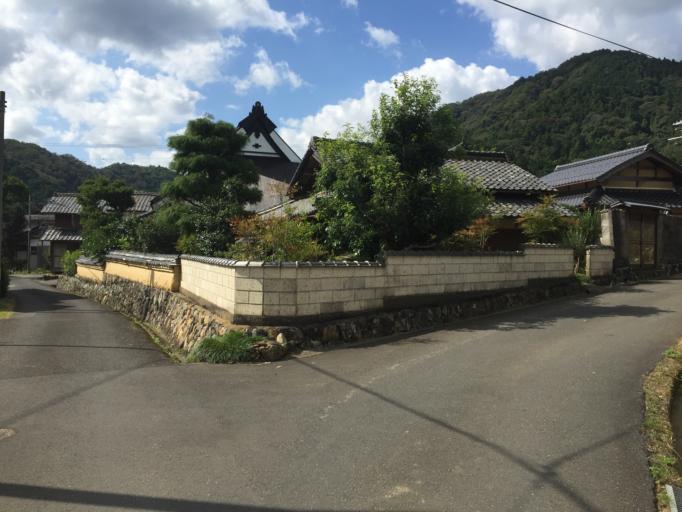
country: JP
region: Kyoto
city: Ayabe
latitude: 35.3411
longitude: 135.1999
